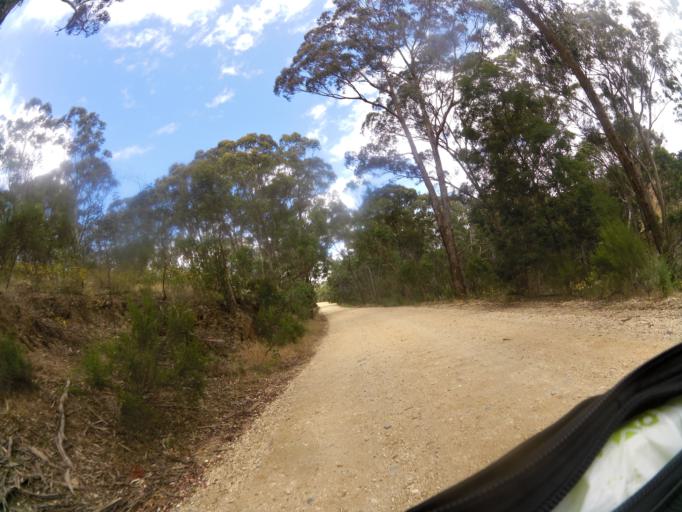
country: AU
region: Victoria
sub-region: Mount Alexander
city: Castlemaine
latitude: -37.0314
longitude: 144.2560
